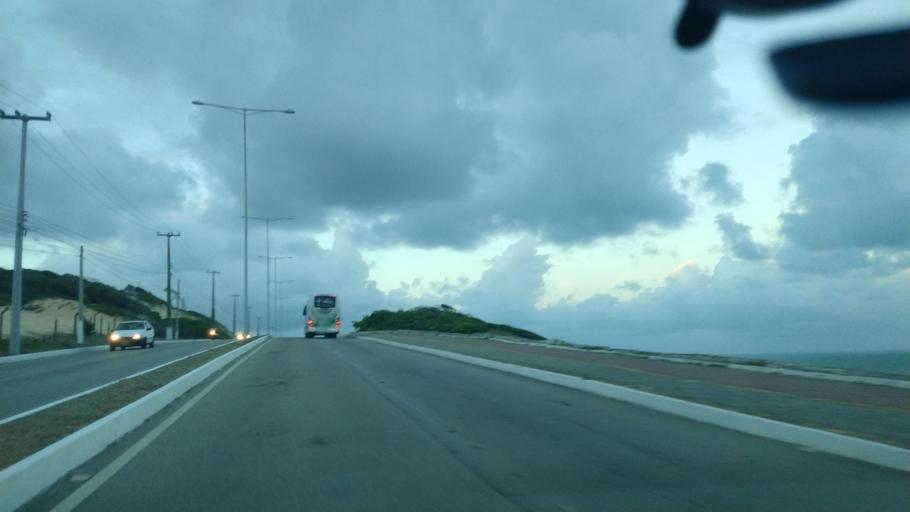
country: BR
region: Rio Grande do Norte
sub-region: Natal
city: Natal
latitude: -5.8215
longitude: -35.1833
